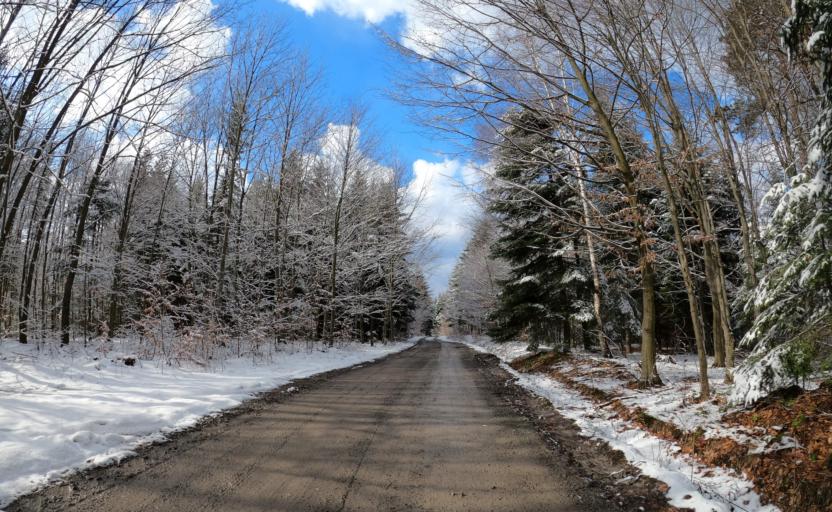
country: PL
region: Subcarpathian Voivodeship
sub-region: Powiat debicki
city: Debica
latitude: 49.9856
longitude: 21.3974
